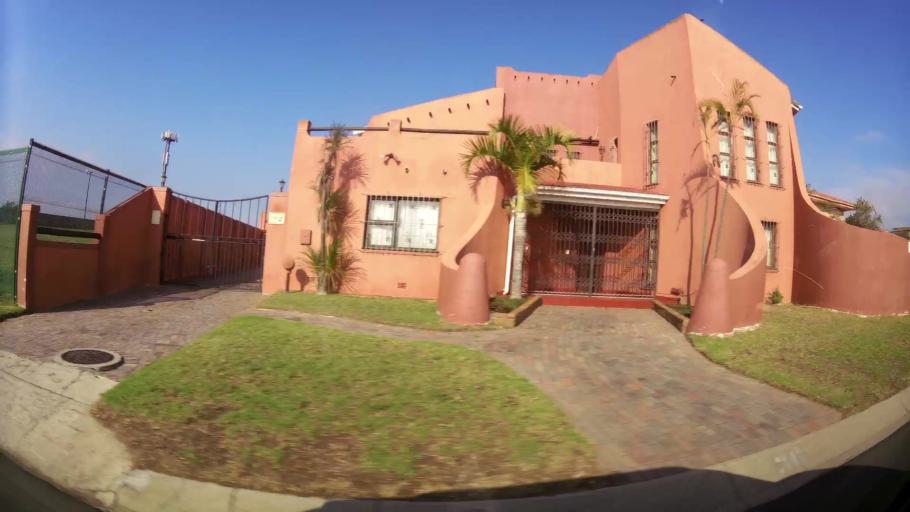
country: ZA
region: Eastern Cape
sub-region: Nelson Mandela Bay Metropolitan Municipality
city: Port Elizabeth
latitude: -33.9264
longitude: 25.5381
